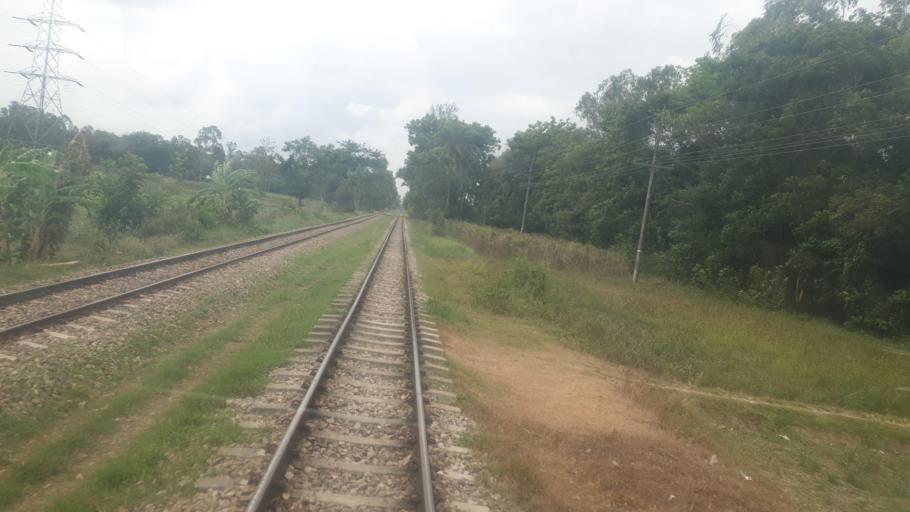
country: BD
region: Chittagong
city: Fatikchari
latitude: 22.7015
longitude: 91.6230
